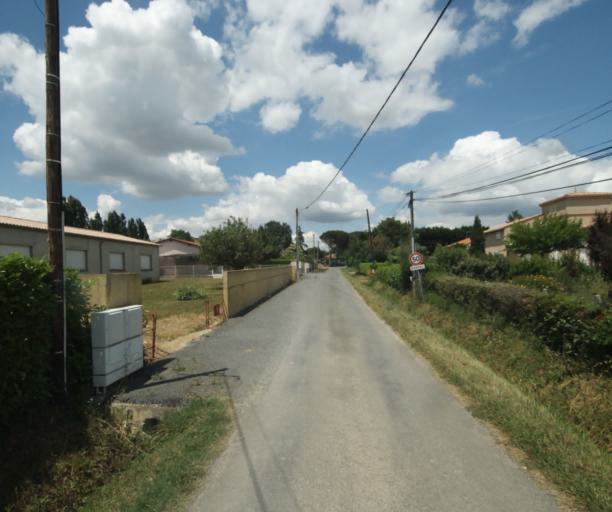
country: FR
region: Midi-Pyrenees
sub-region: Departement du Tarn
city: Soual
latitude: 43.5394
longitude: 2.0624
